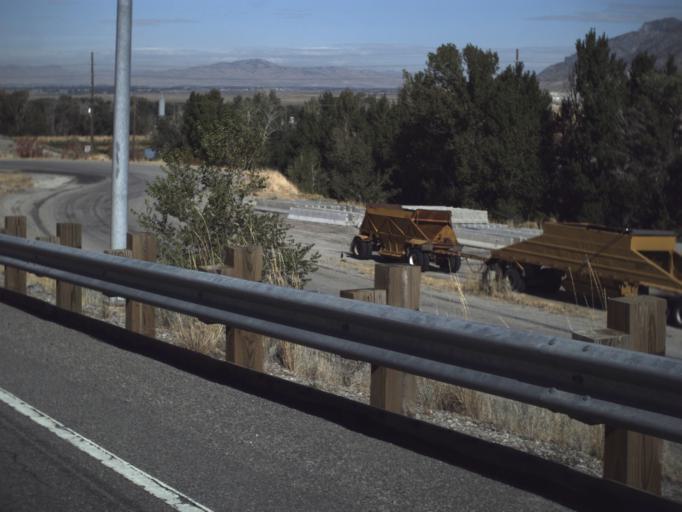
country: US
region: Utah
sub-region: Box Elder County
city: Brigham City
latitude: 41.5011
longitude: -111.9963
